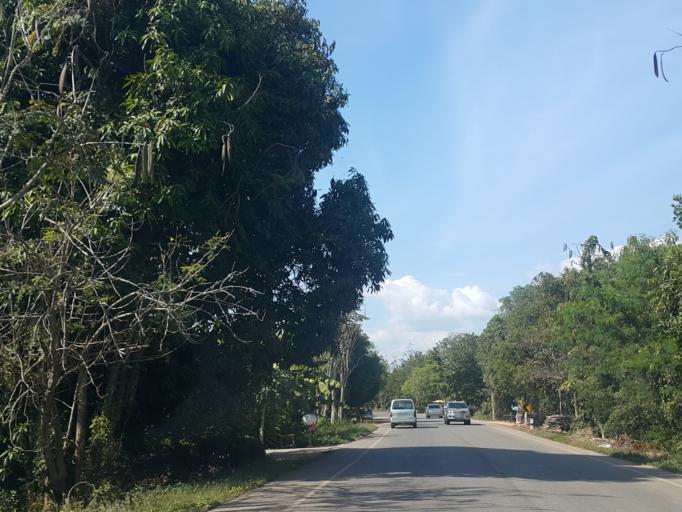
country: TH
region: Sukhothai
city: Sawankhalok
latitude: 17.2665
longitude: 99.8338
